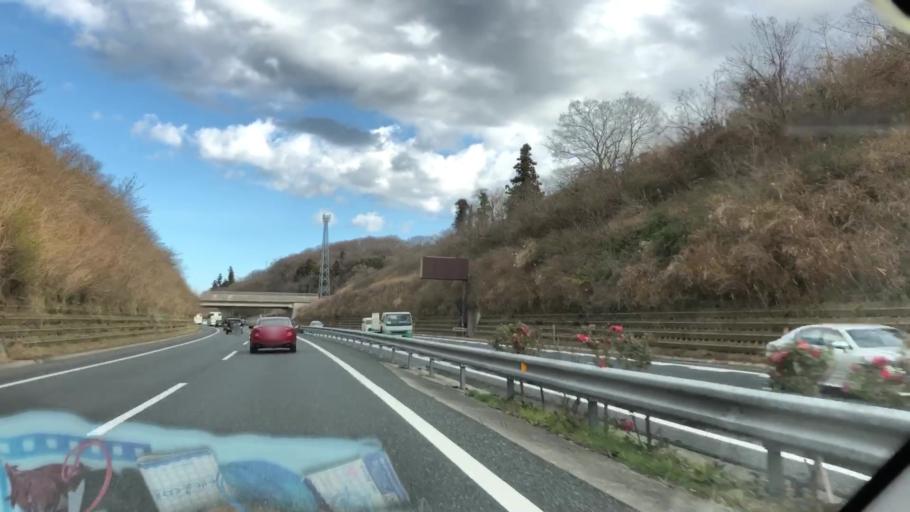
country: JP
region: Chiba
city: Kimitsu
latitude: 35.3241
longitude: 139.9456
